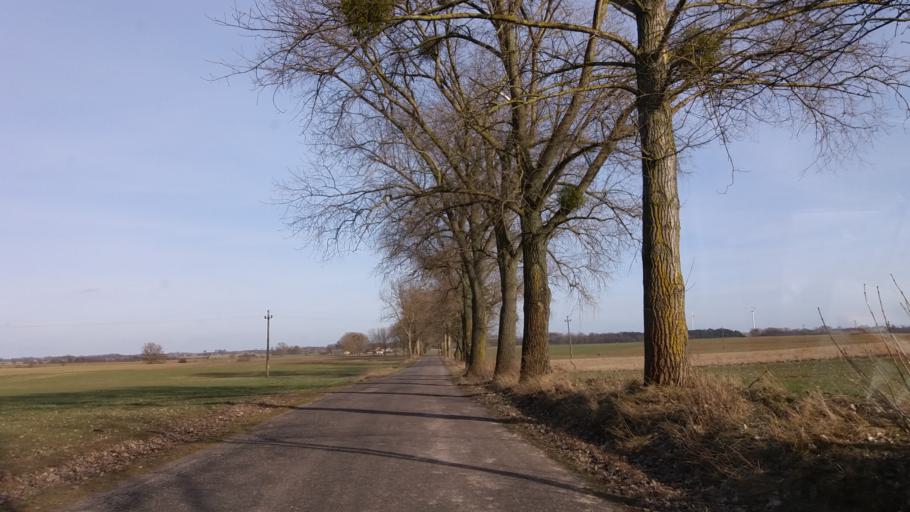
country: PL
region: West Pomeranian Voivodeship
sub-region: Powiat choszczenski
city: Choszczno
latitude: 53.1280
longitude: 15.3877
